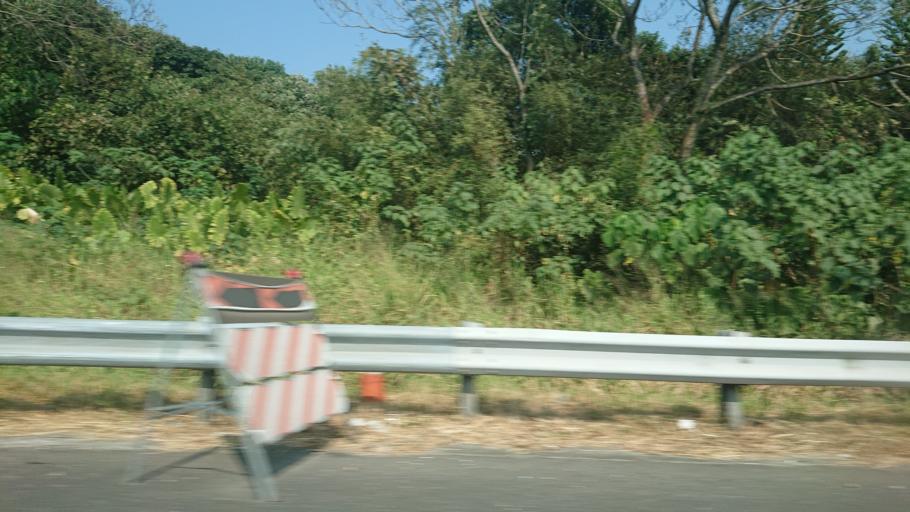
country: TW
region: Taiwan
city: Lugu
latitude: 23.7775
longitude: 120.6716
